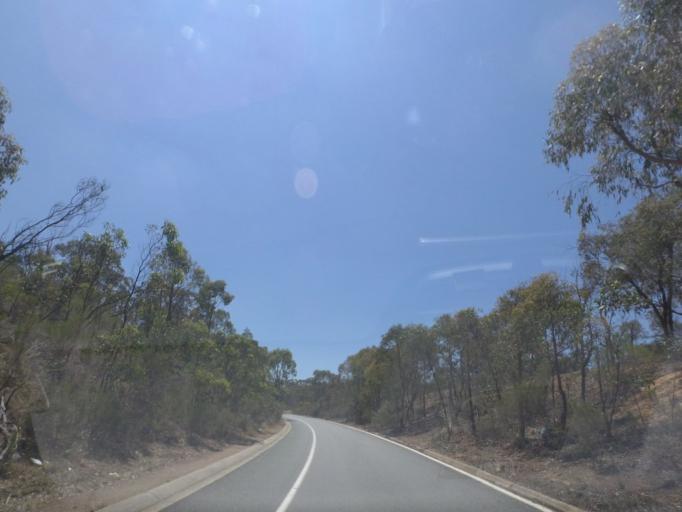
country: AU
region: Victoria
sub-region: Murrindindi
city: Kinglake West
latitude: -36.9624
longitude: 145.1822
